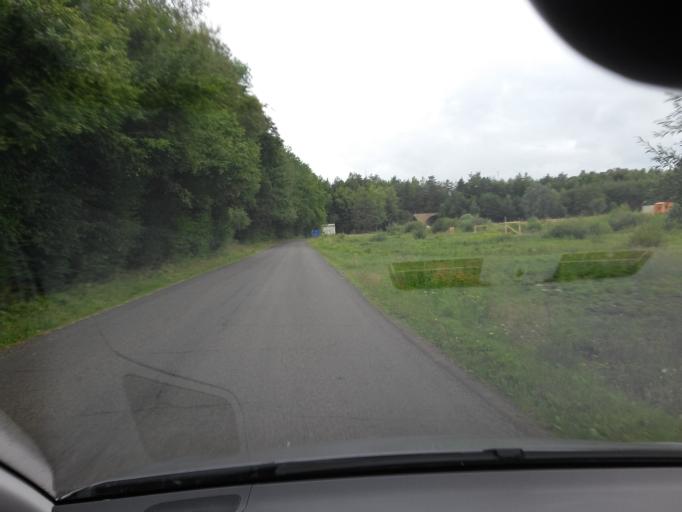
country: BE
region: Wallonia
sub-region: Province du Luxembourg
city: Attert
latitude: 49.7214
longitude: 5.8039
